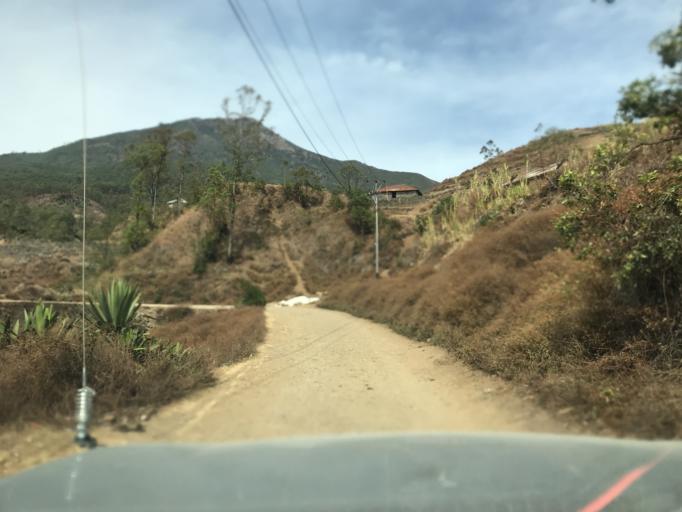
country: TL
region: Ainaro
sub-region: Ainaro
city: Ainaro
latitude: -8.8982
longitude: 125.5178
